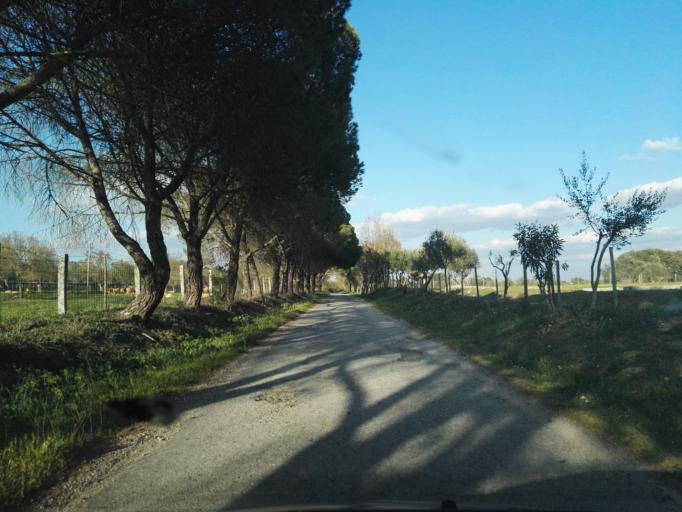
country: PT
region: Evora
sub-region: Evora
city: Evora
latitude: 38.5345
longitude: -7.9442
